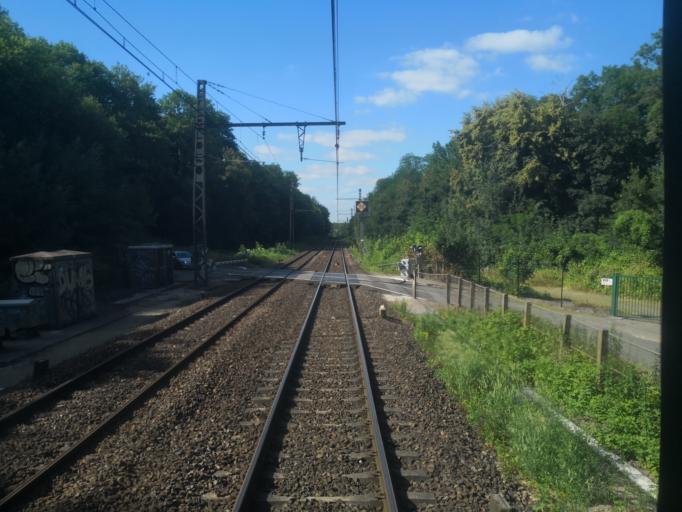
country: FR
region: Ile-de-France
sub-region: Departement de Seine-et-Marne
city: La Rochette
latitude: 48.5034
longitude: 2.6683
